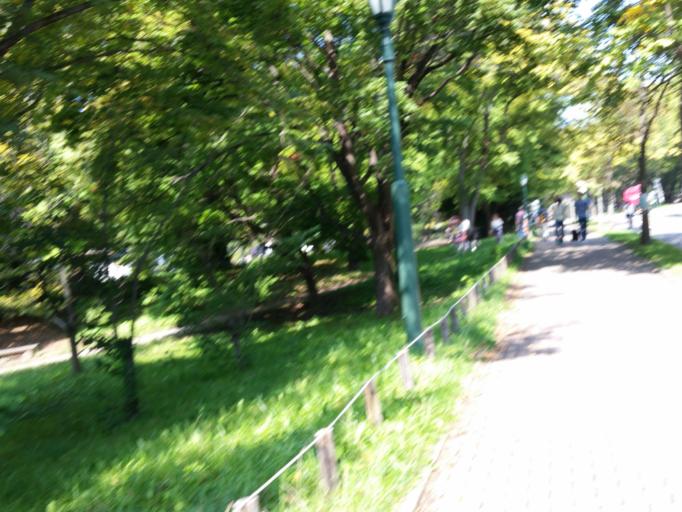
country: JP
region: Hokkaido
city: Sapporo
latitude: 43.0744
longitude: 141.3422
